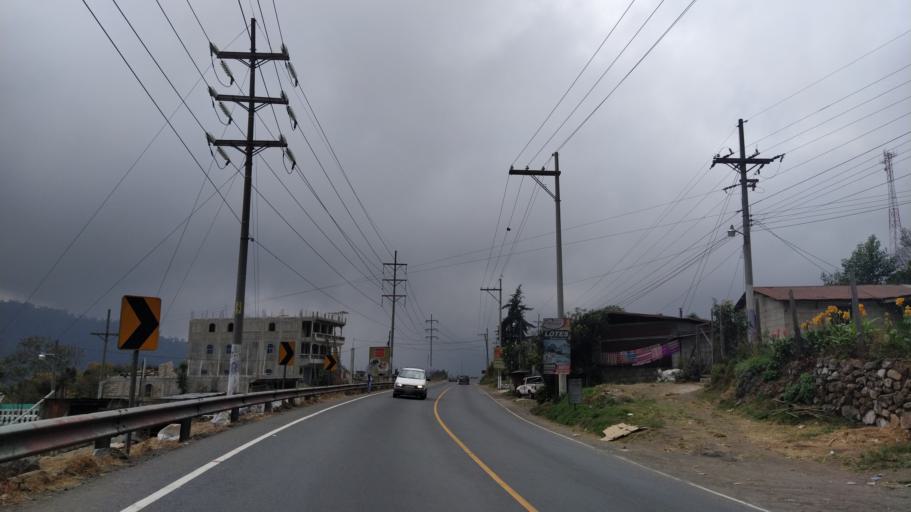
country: GT
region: Quetzaltenango
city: Zunil
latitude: 14.7485
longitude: -91.5105
